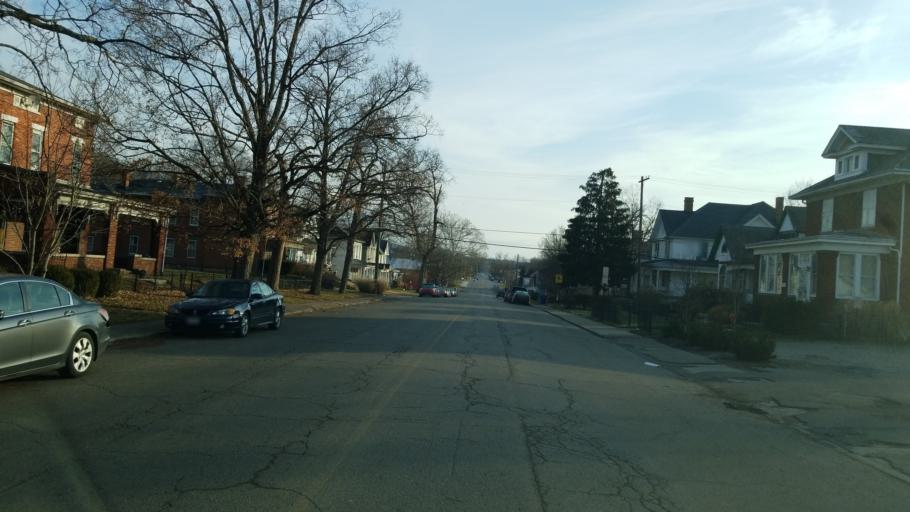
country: US
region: Ohio
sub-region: Ross County
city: Chillicothe
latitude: 39.3365
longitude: -82.9789
